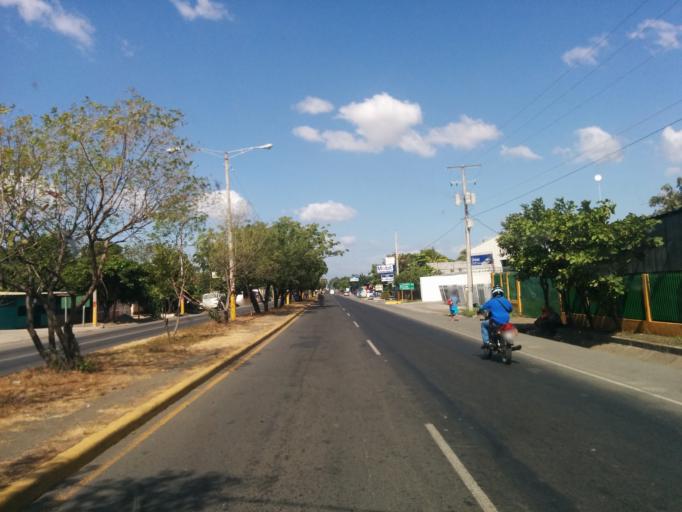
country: NI
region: Managua
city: Tipitapa
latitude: 12.1967
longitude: -86.1039
